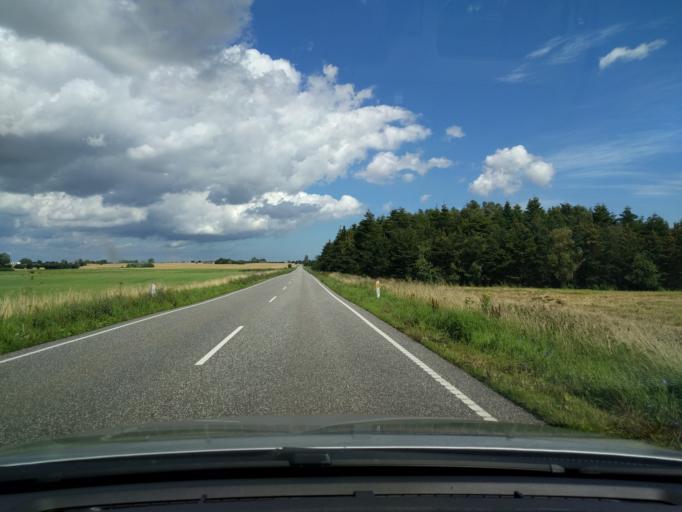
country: DK
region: Zealand
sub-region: Guldborgsund Kommune
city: Stubbekobing
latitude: 54.9059
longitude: 12.1236
